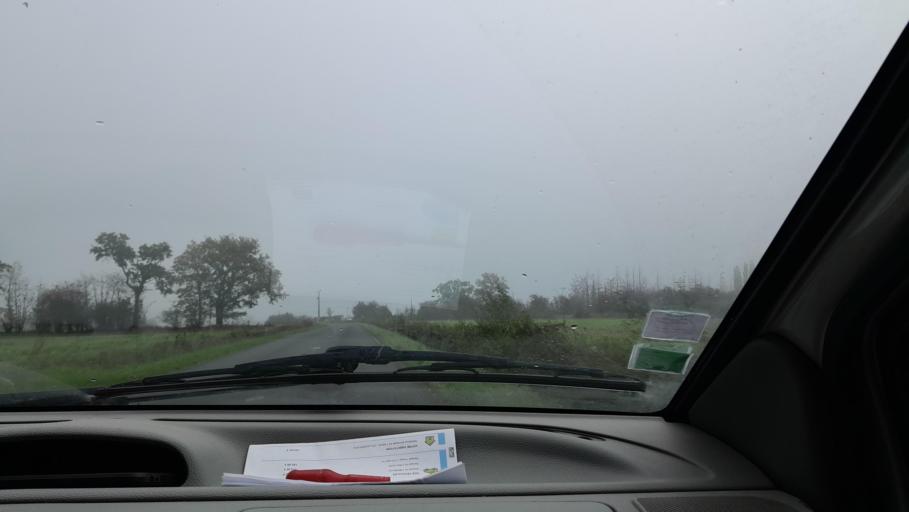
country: FR
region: Pays de la Loire
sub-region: Departement de la Mayenne
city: Saint-Pierre-la-Cour
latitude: 48.1273
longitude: -1.0235
